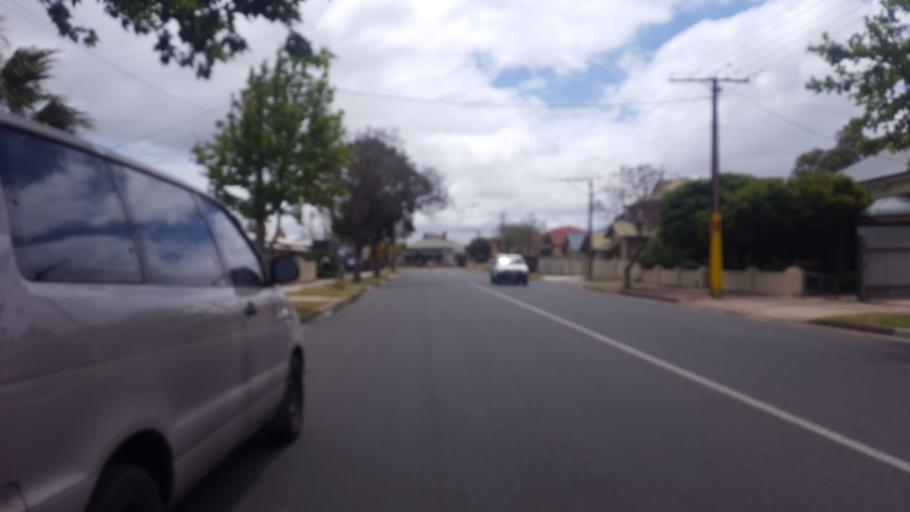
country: AU
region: South Australia
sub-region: Port Adelaide Enfield
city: Alberton
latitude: -34.8579
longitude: 138.5224
